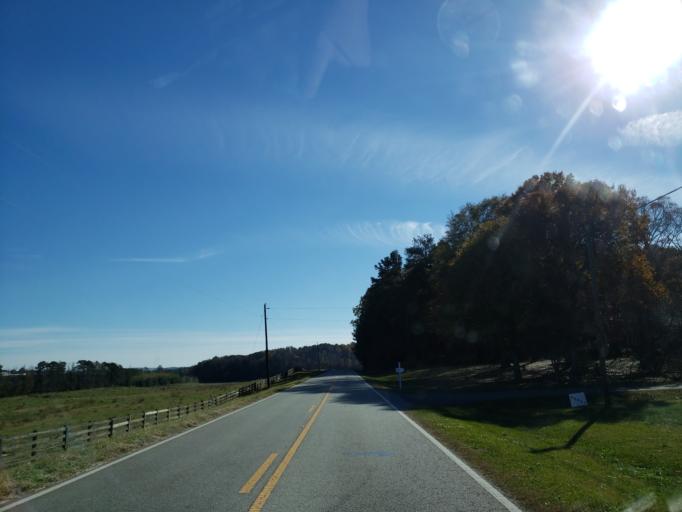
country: US
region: Alabama
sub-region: Cleburne County
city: Heflin
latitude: 33.5781
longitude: -85.6394
